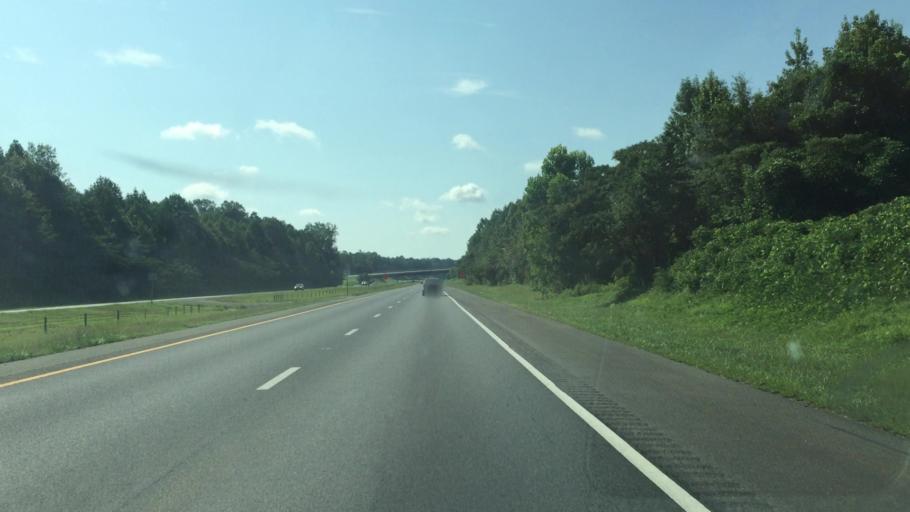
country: US
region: North Carolina
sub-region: Mecklenburg County
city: Mint Hill
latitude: 35.2079
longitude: -80.6395
